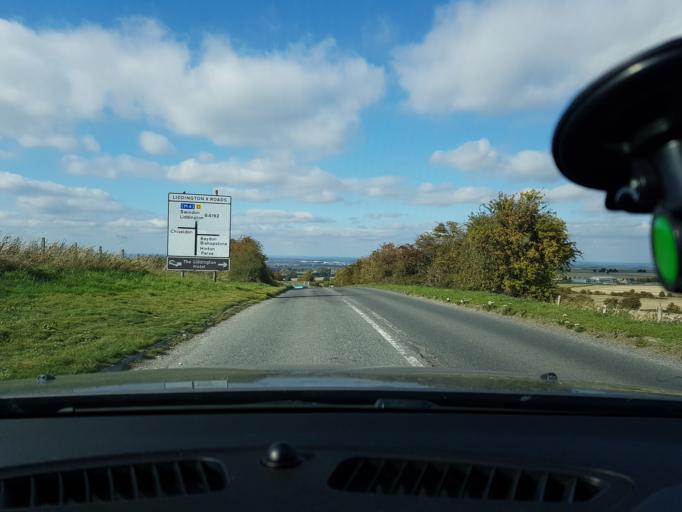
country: GB
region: England
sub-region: Borough of Swindon
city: Wanborough
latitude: 51.5223
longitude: -1.6865
